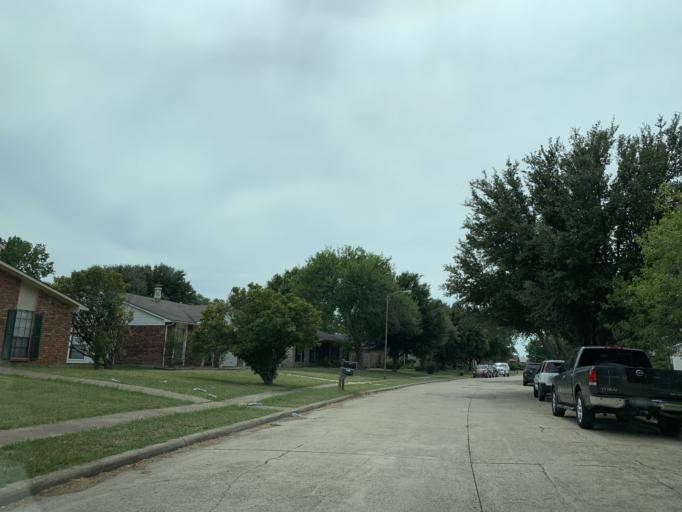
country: US
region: Texas
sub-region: Dallas County
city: Cedar Hill
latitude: 32.6490
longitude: -97.0316
